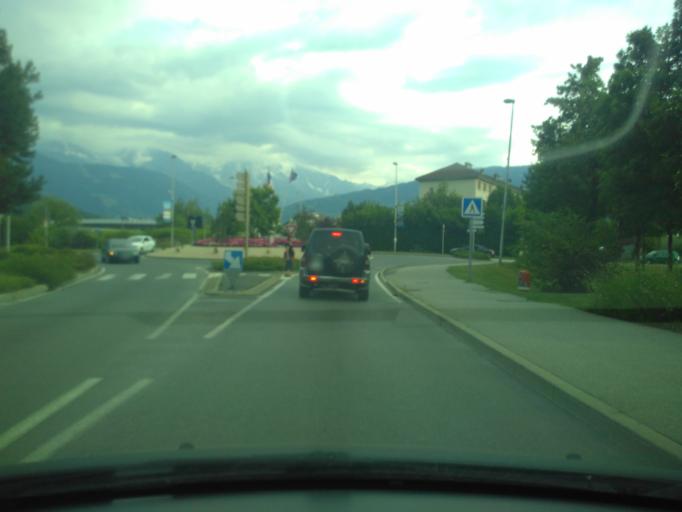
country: FR
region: Rhone-Alpes
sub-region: Departement de la Haute-Savoie
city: Sallanches
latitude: 45.9400
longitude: 6.6401
